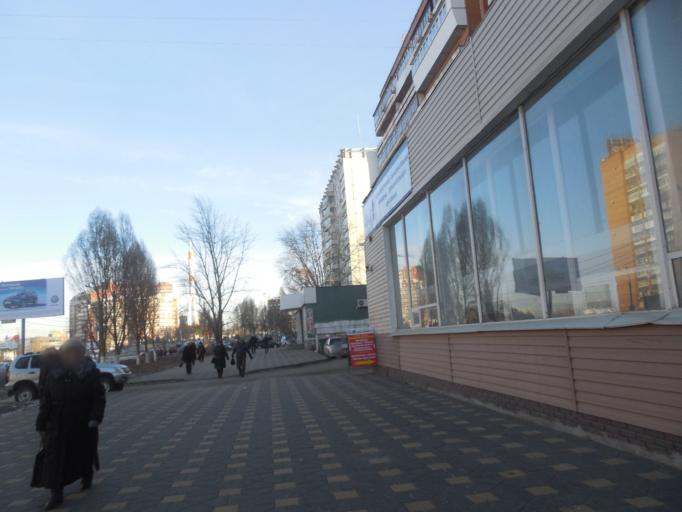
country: RU
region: Samara
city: Samara
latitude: 53.2106
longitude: 50.1423
